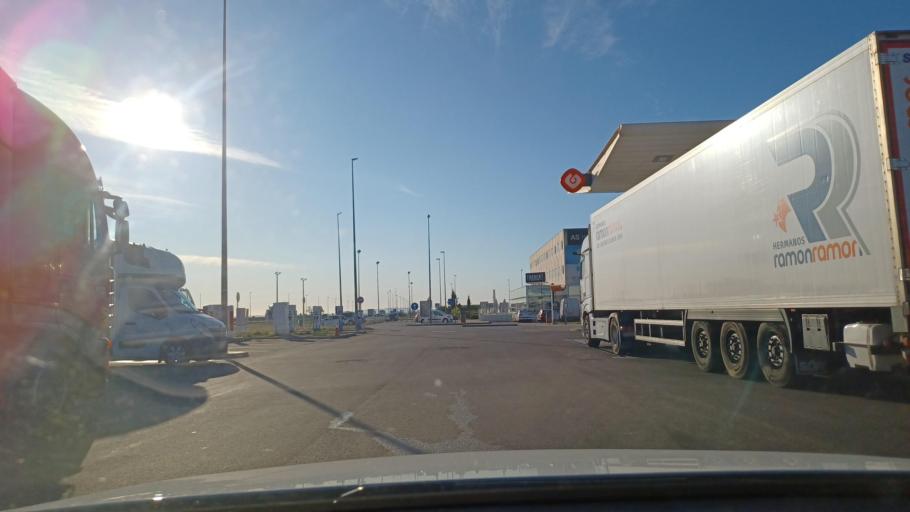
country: ES
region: Valencia
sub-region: Provincia de Valencia
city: Torrent
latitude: 39.4009
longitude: -0.4935
